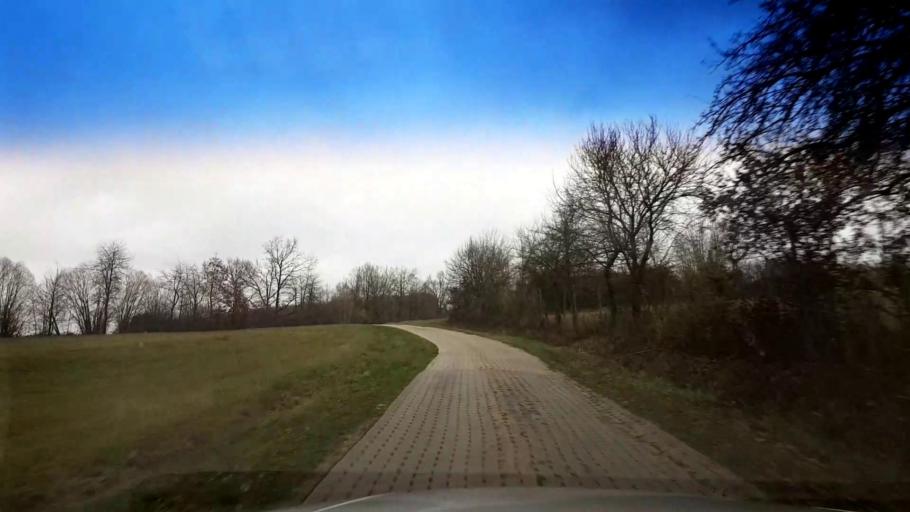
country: DE
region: Bavaria
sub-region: Upper Franconia
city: Zapfendorf
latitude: 50.0004
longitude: 10.9440
